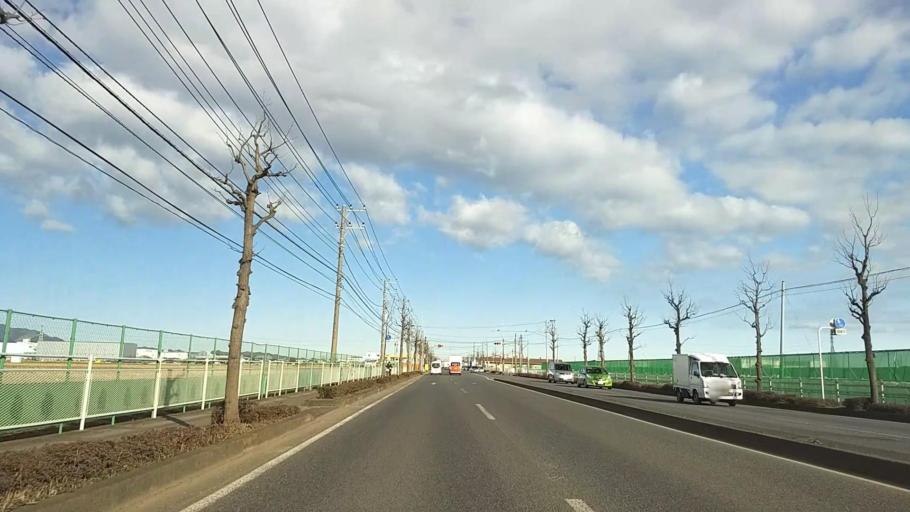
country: JP
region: Kanagawa
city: Atsugi
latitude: 35.3906
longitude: 139.3616
